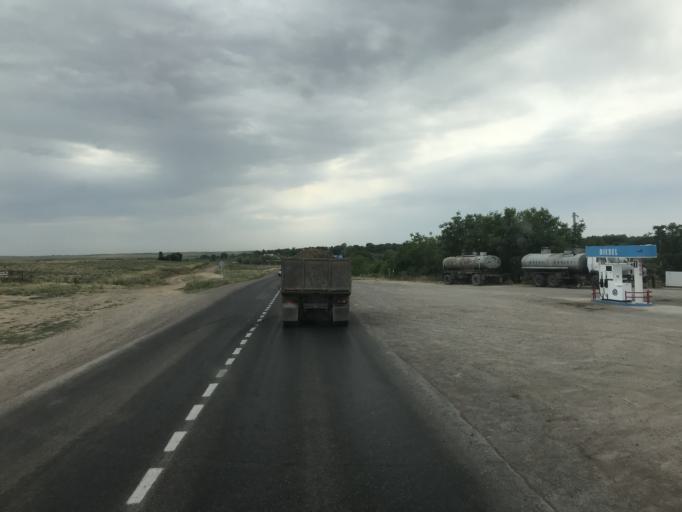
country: KZ
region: Ongtustik Qazaqstan
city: Saryaghash
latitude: 41.3958
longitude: 69.0395
